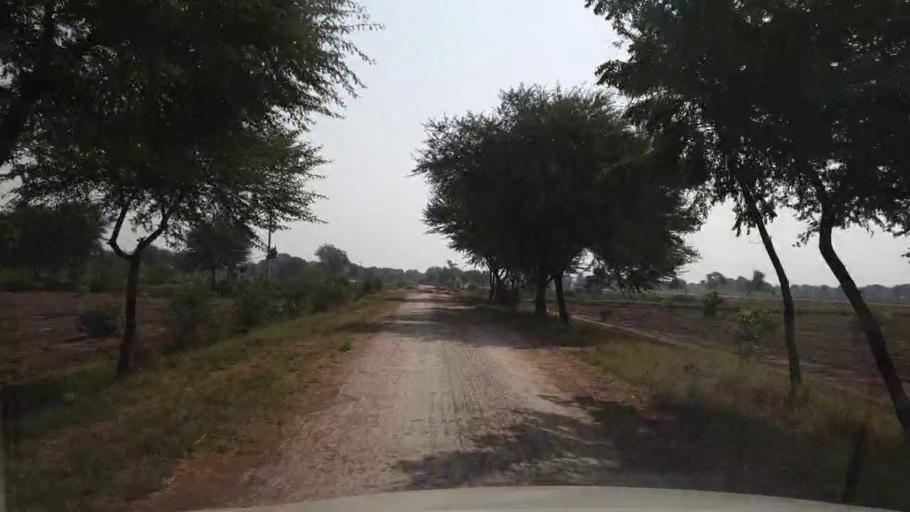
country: PK
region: Sindh
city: Chor
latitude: 25.4618
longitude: 69.7108
